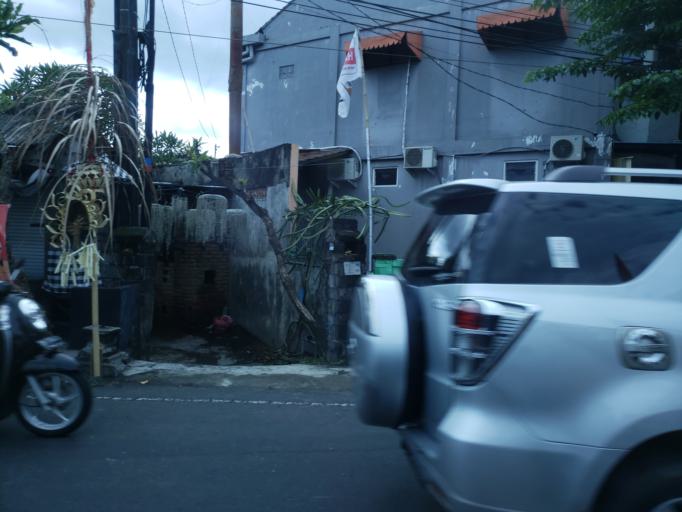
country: ID
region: Bali
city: Dajan Tangluk
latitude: -8.6473
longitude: 115.2424
